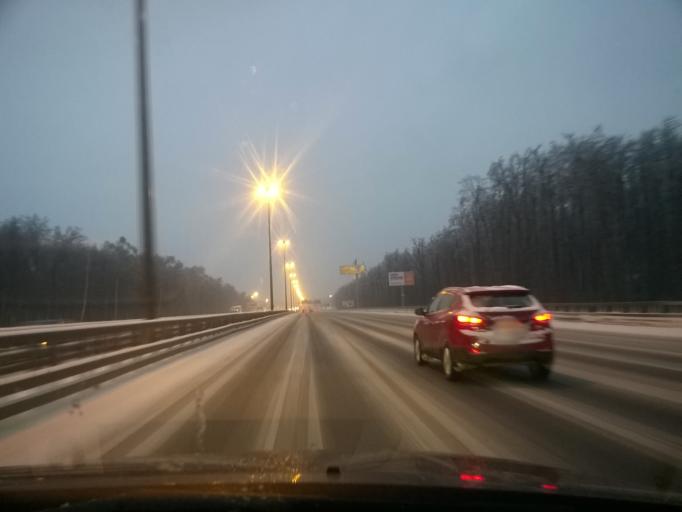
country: RU
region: Moskovskaya
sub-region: Leninskiy Rayon
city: Vnukovo
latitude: 55.5942
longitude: 37.2976
